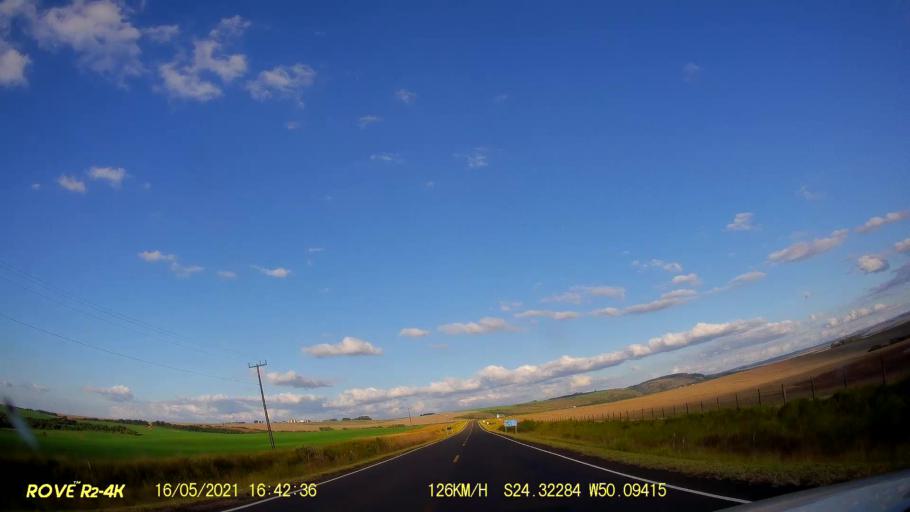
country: BR
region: Parana
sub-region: Pirai Do Sul
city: Pirai do Sul
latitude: -24.3234
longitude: -50.0939
